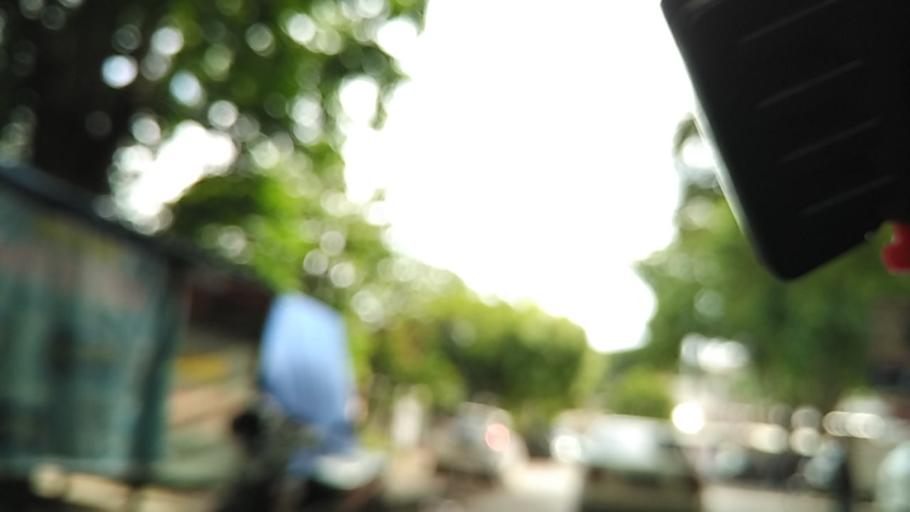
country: ID
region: Central Java
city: Semarang
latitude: -6.9976
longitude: 110.4245
